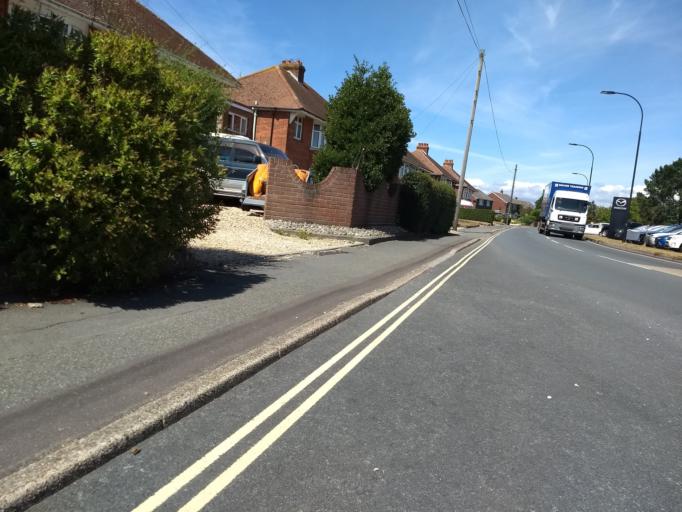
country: GB
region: England
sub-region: Isle of Wight
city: Northwood
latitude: 50.7394
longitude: -1.3082
